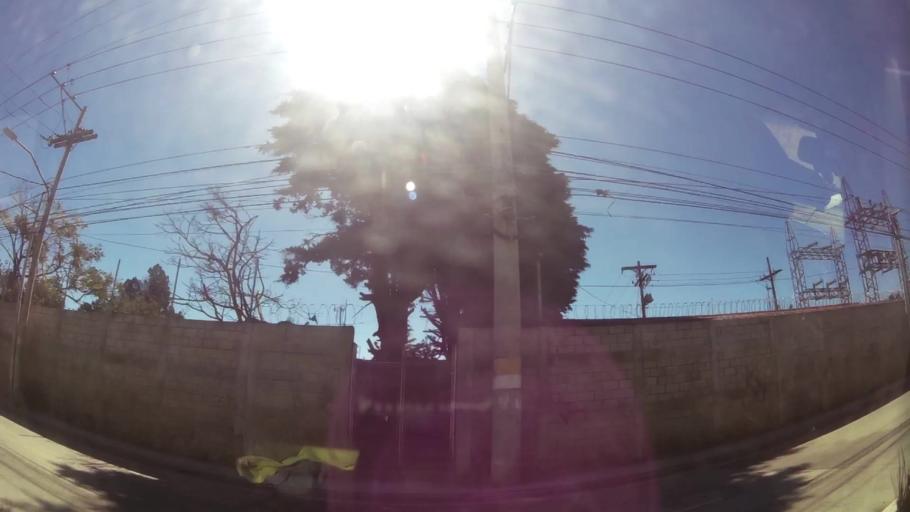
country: GT
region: Guatemala
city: San Jose Pinula
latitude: 14.5446
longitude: -90.4293
